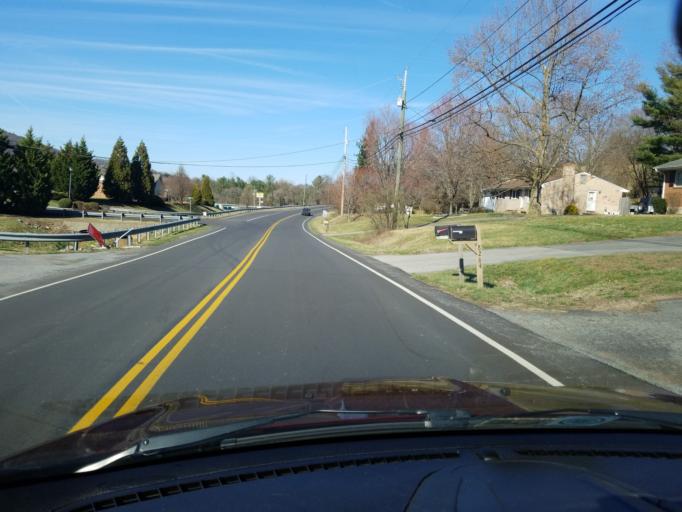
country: US
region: Virginia
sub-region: Botetourt County
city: Cloverdale
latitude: 37.3562
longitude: -79.9131
